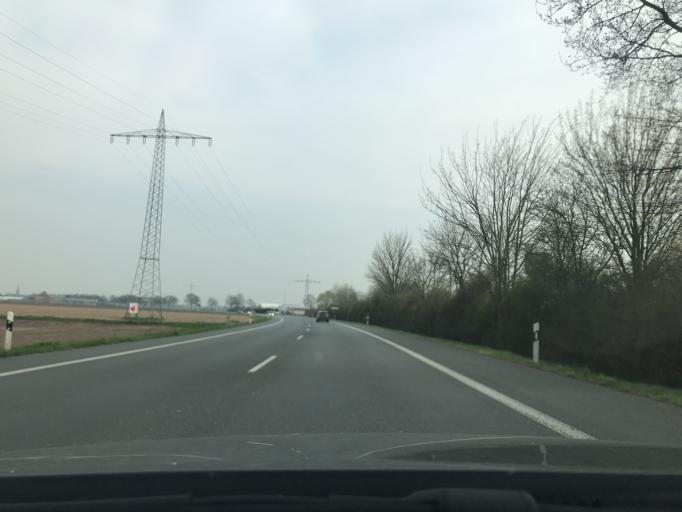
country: DE
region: North Rhine-Westphalia
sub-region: Regierungsbezirk Dusseldorf
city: Wachtendonk
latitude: 51.4531
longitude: 6.3859
